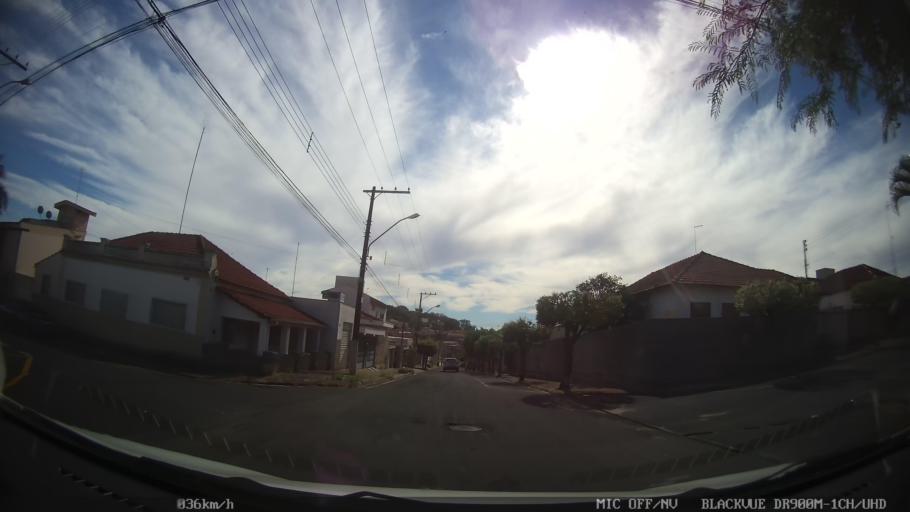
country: BR
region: Sao Paulo
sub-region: Catanduva
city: Catanduva
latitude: -21.1316
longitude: -48.9652
